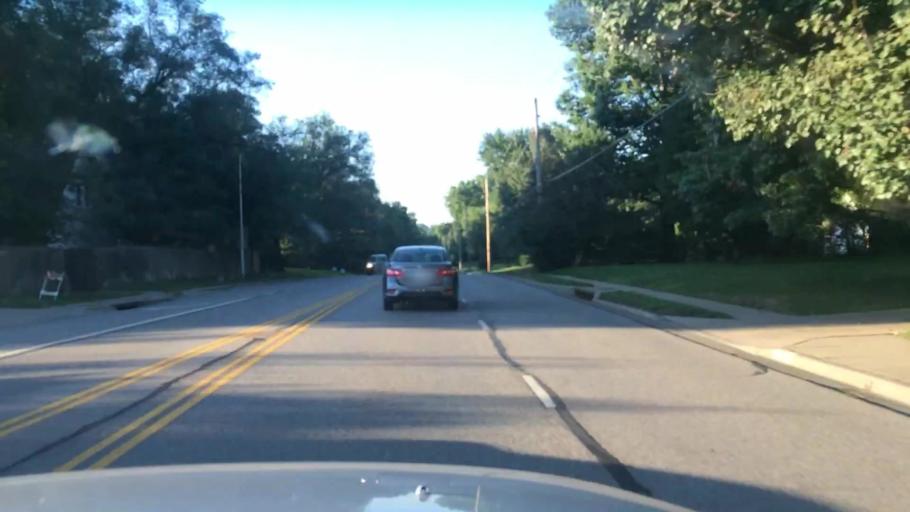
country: US
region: Kansas
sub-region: Johnson County
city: Prairie Village
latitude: 39.0069
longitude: -94.6491
